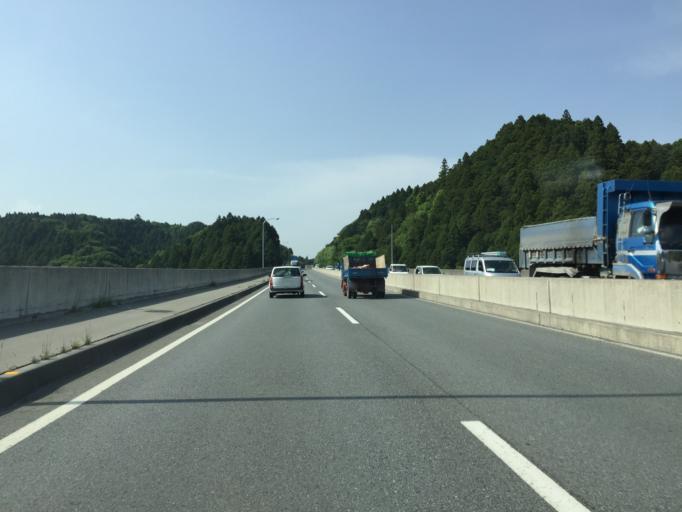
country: JP
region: Fukushima
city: Iwaki
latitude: 37.0125
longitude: 140.8959
